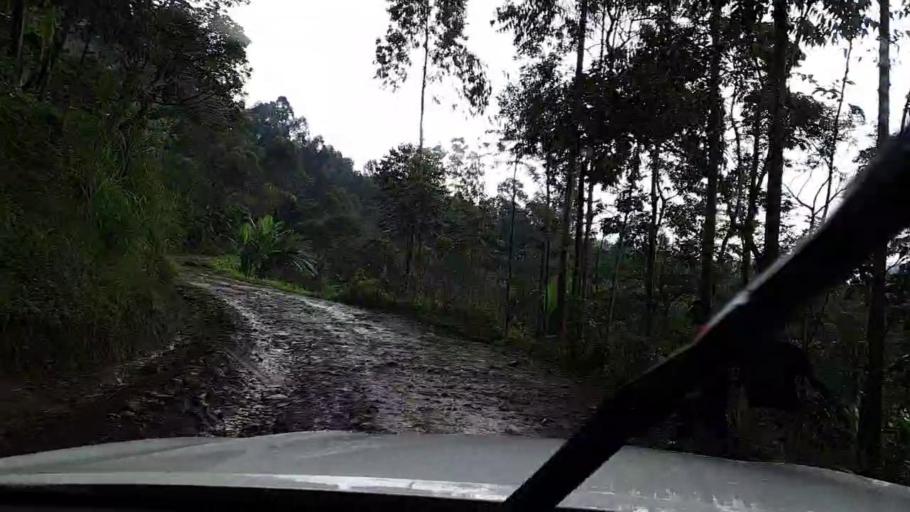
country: RW
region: Western Province
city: Cyangugu
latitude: -2.5189
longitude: 29.0441
